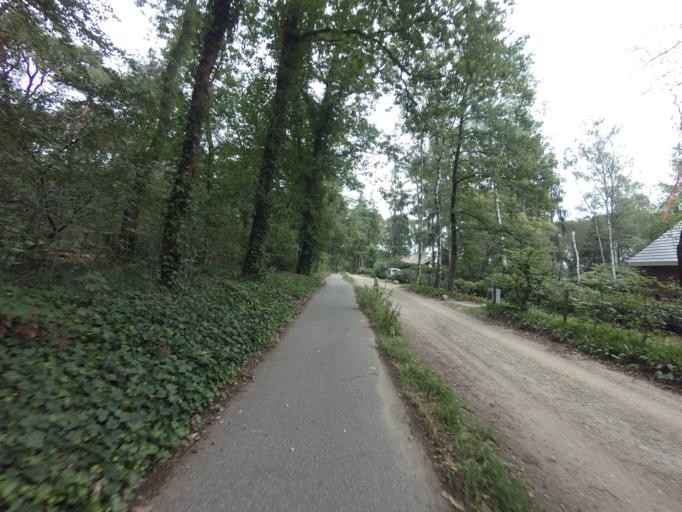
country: NL
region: Overijssel
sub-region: Gemeente Hof van Twente
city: Markelo
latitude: 52.2911
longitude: 6.4261
